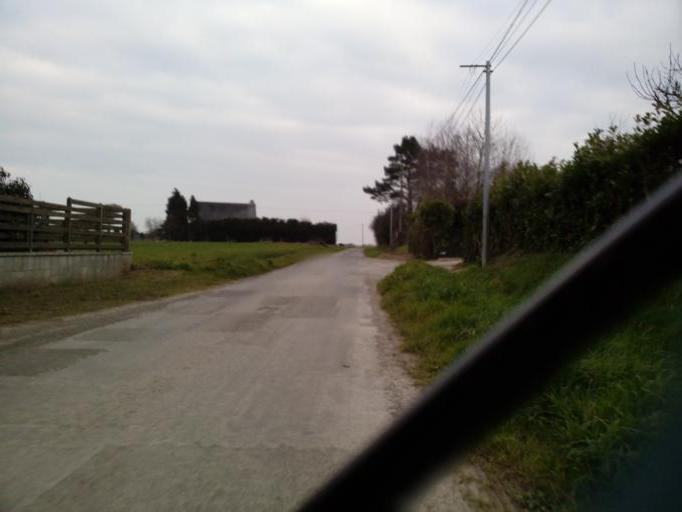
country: FR
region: Brittany
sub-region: Departement d'Ille-et-Vilaine
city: Breteil
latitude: 48.1178
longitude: -1.8990
